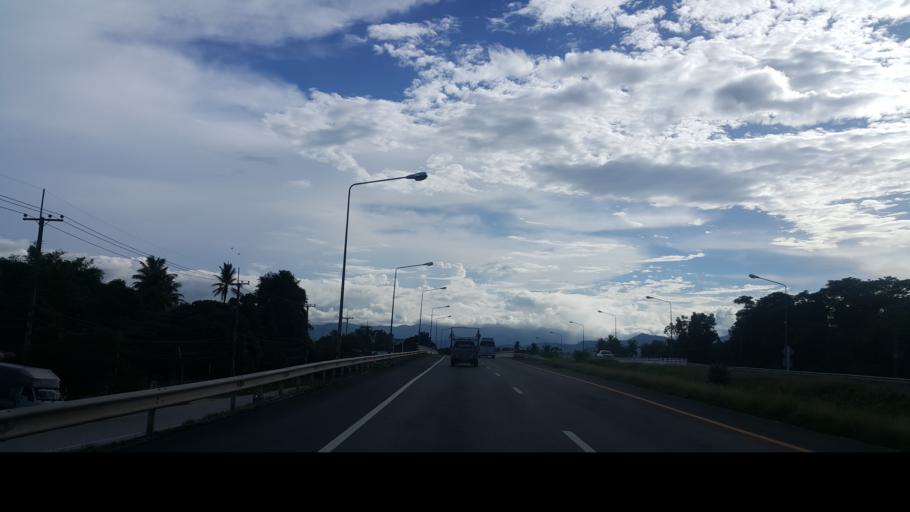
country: TH
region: Tak
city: Ban Tak
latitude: 17.1098
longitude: 99.0820
